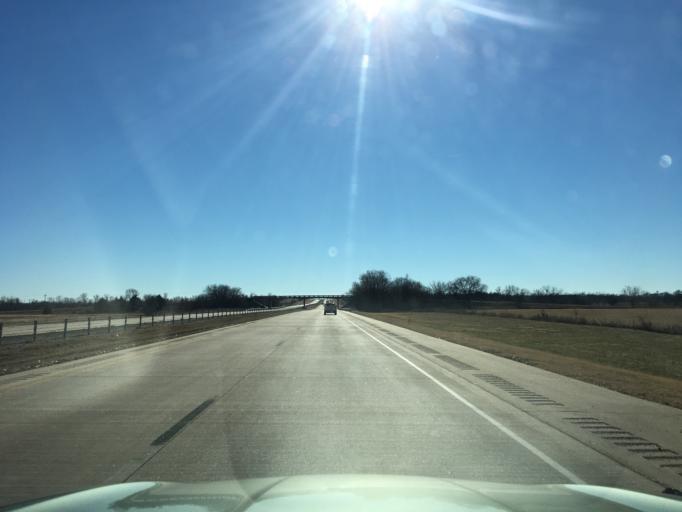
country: US
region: Oklahoma
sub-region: Noble County
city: Perry
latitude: 36.4664
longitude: -97.3271
